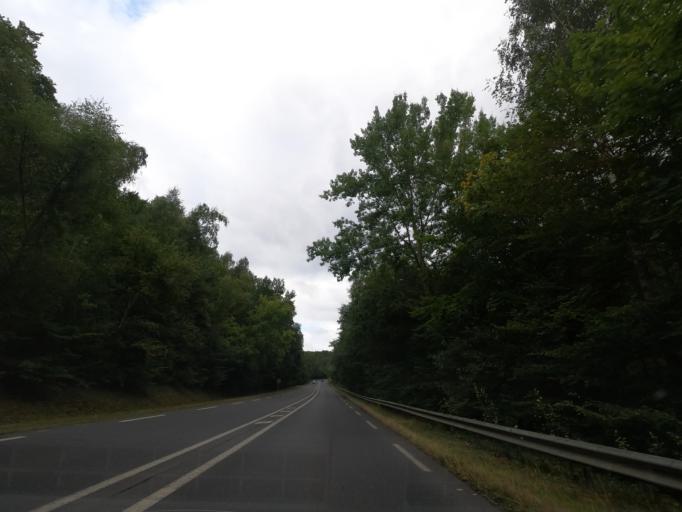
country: FR
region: Haute-Normandie
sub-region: Departement de la Seine-Maritime
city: Sahurs
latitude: 49.3359
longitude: 0.9197
